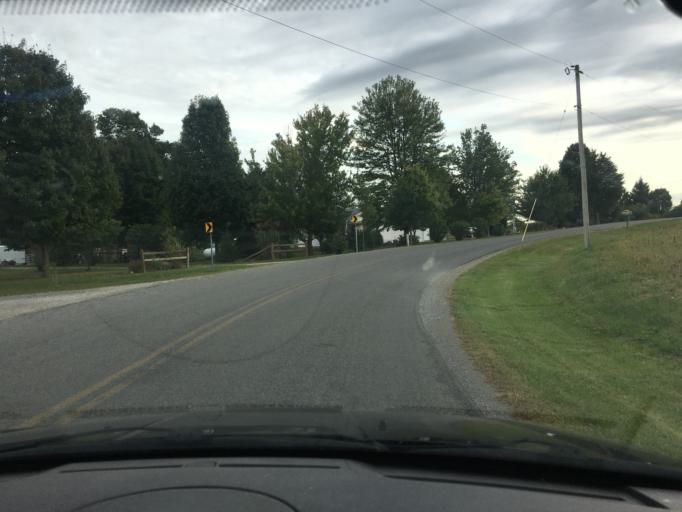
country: US
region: Ohio
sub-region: Logan County
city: West Liberty
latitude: 40.2916
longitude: -83.6844
